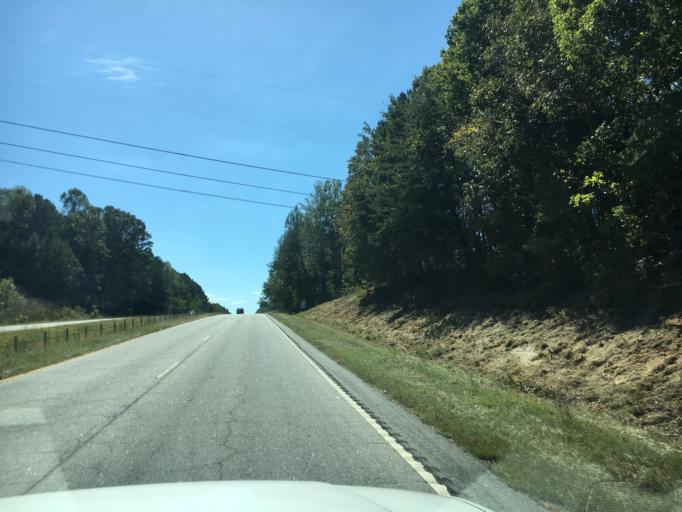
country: US
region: South Carolina
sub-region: Pickens County
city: Liberty
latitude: 34.7388
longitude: -82.7193
